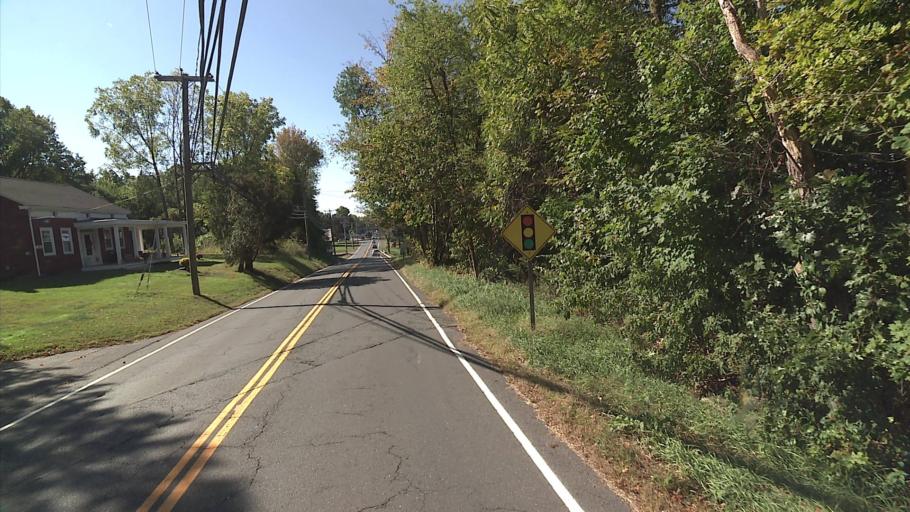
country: US
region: Connecticut
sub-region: Tolland County
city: Ellington
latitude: 41.9025
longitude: -72.4579
